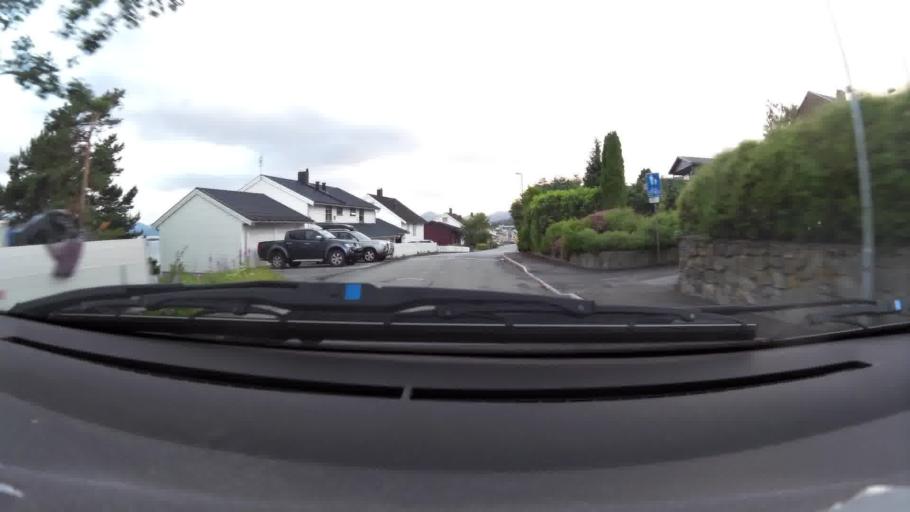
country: NO
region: More og Romsdal
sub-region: Molde
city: Molde
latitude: 62.7416
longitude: 7.1851
